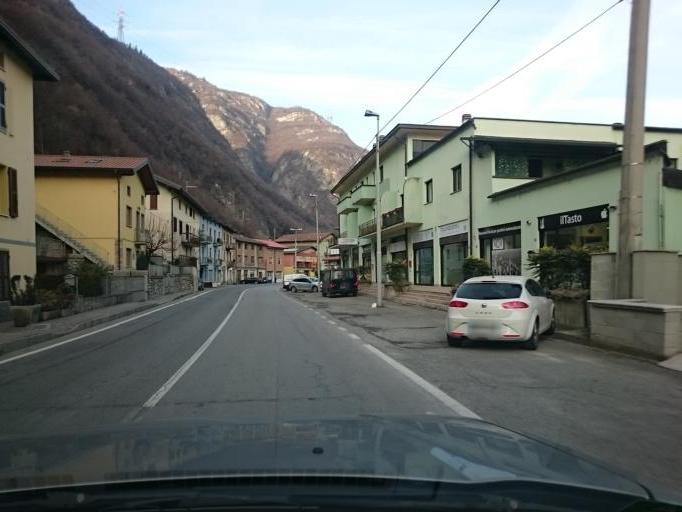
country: IT
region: Lombardy
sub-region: Provincia di Brescia
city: Esine
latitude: 45.9303
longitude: 10.2408
